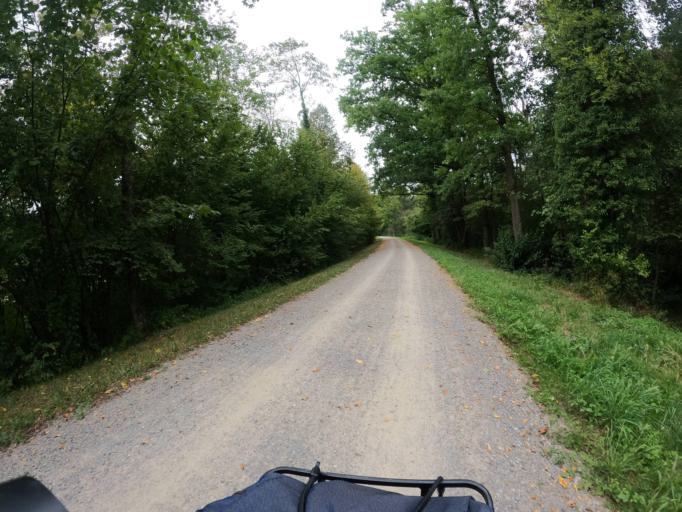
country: CH
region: Zurich
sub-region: Bezirk Affoltern
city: Ottenbach
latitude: 47.2707
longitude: 8.4003
